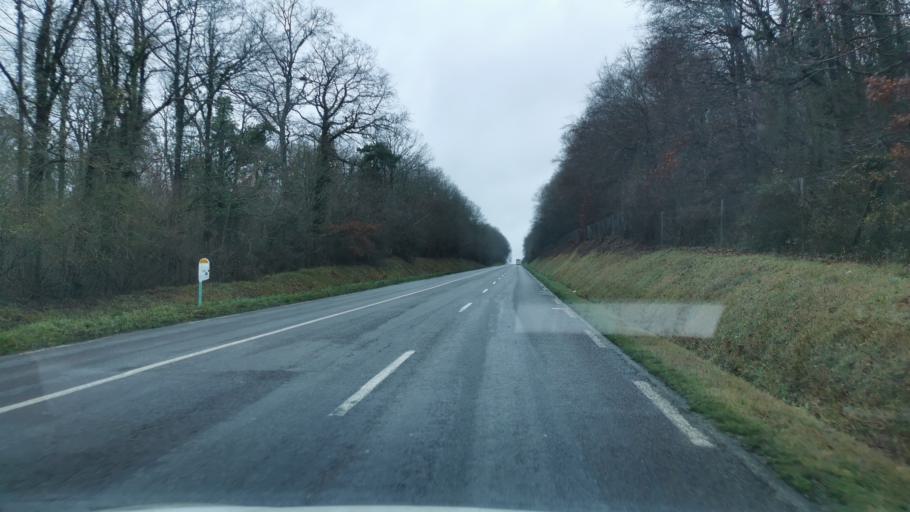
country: FR
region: Haute-Normandie
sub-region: Departement de l'Eure
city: Normanville
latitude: 49.0723
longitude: 1.1755
